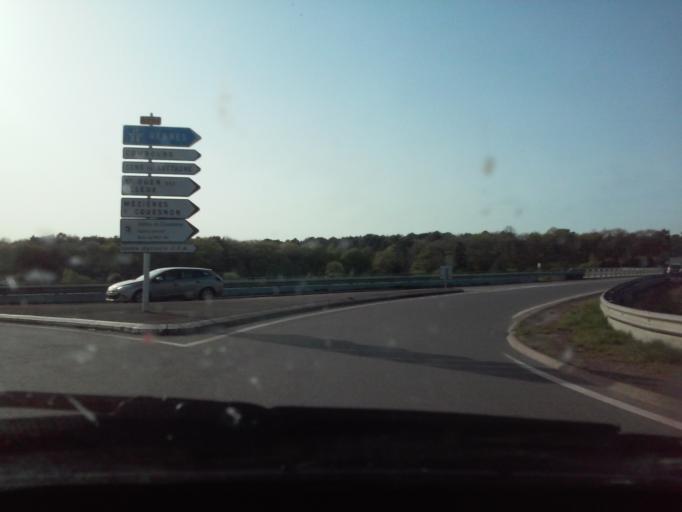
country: FR
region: Brittany
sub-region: Departement d'Ille-et-Vilaine
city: Saint-Aubin-du-Cormier
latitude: 48.2625
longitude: -1.4108
